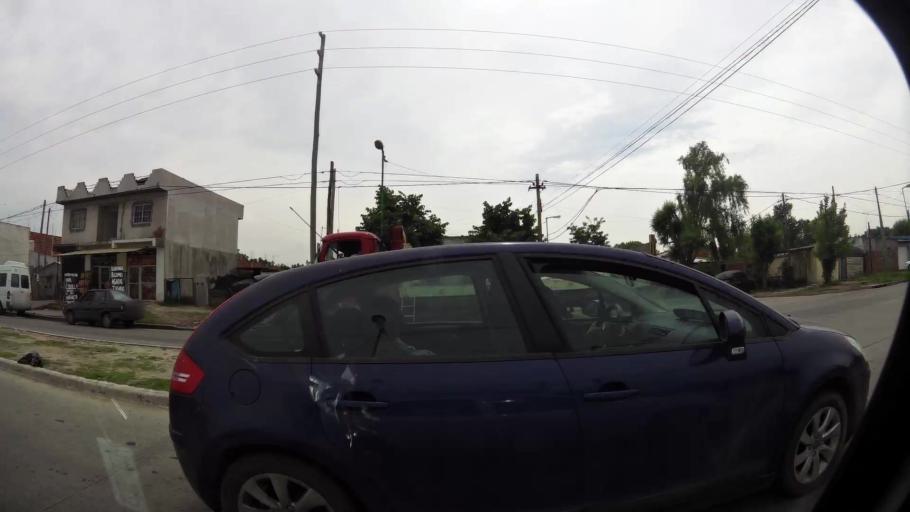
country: AR
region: Buenos Aires
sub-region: Partido de La Plata
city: La Plata
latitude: -34.9305
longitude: -58.0121
